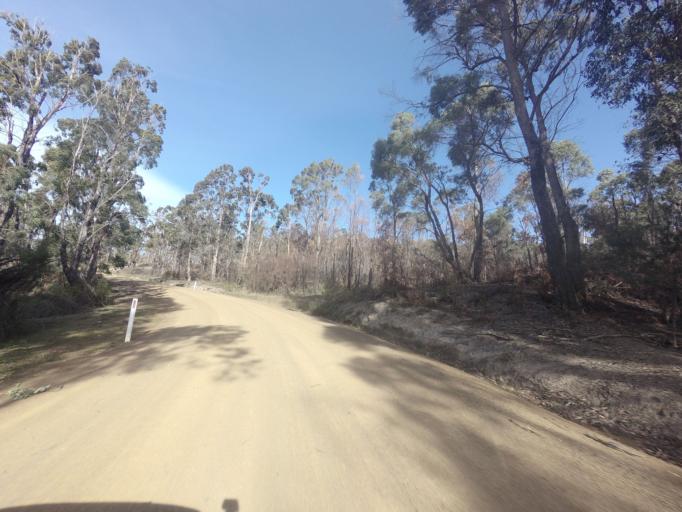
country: AU
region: Tasmania
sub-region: Kingborough
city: Kettering
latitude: -43.0814
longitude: 147.2633
